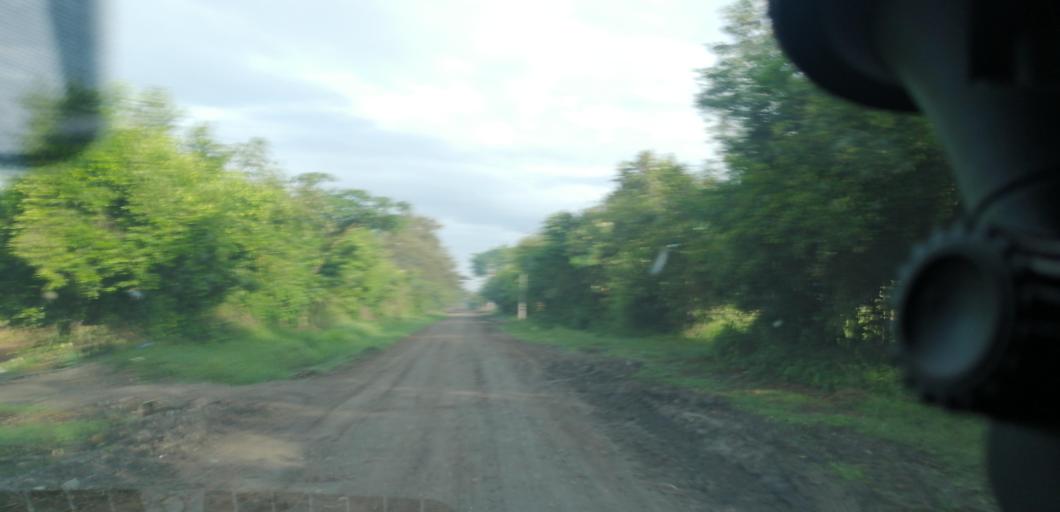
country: CO
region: Valle del Cauca
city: Palmira
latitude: 3.5411
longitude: -76.3599
